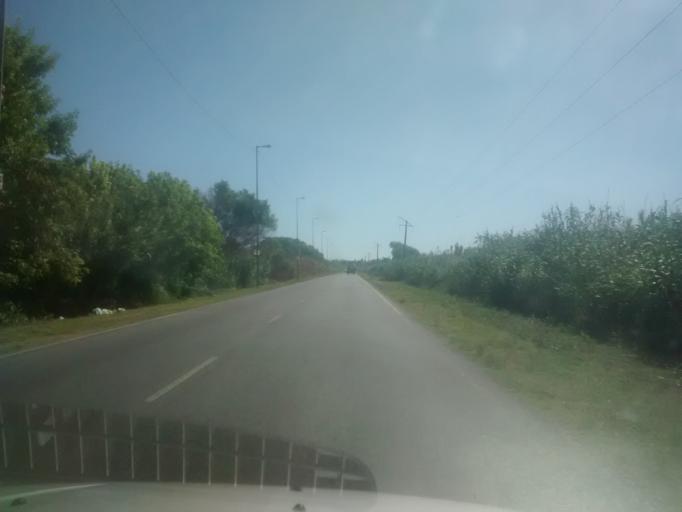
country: AR
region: Buenos Aires
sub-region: Partido de Berisso
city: Berisso
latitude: -34.9061
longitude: -57.9056
